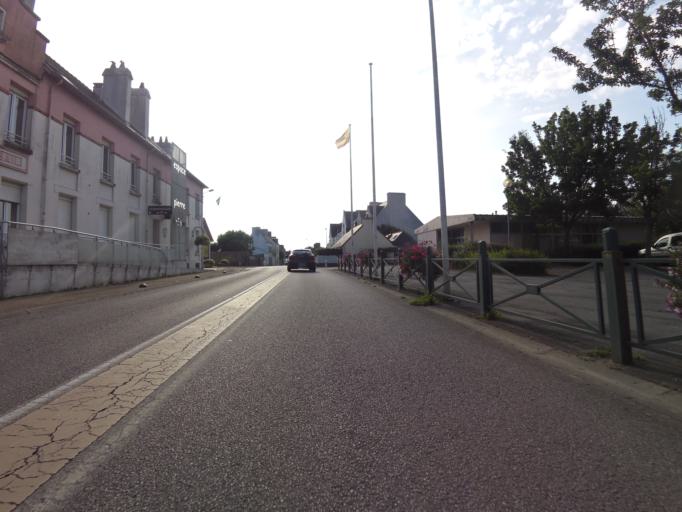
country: FR
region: Brittany
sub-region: Departement du Finistere
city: Plozevet
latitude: 47.9856
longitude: -4.4200
